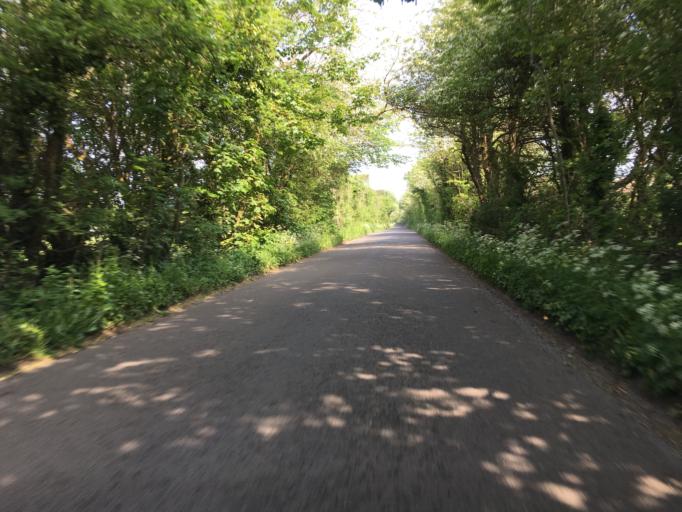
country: GB
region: England
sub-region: North Somerset
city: Brockley
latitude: 51.4043
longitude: -2.7162
